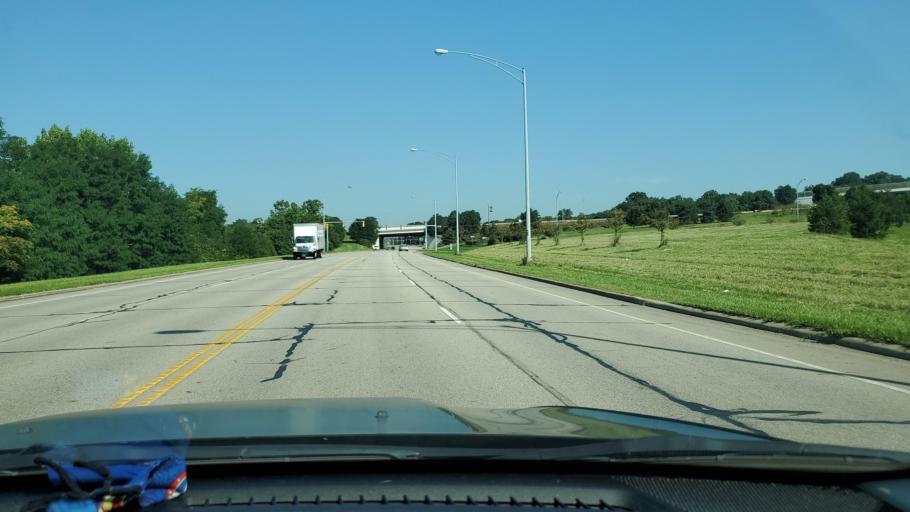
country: US
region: Ohio
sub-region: Mahoning County
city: Youngstown
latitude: 41.1212
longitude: -80.6755
